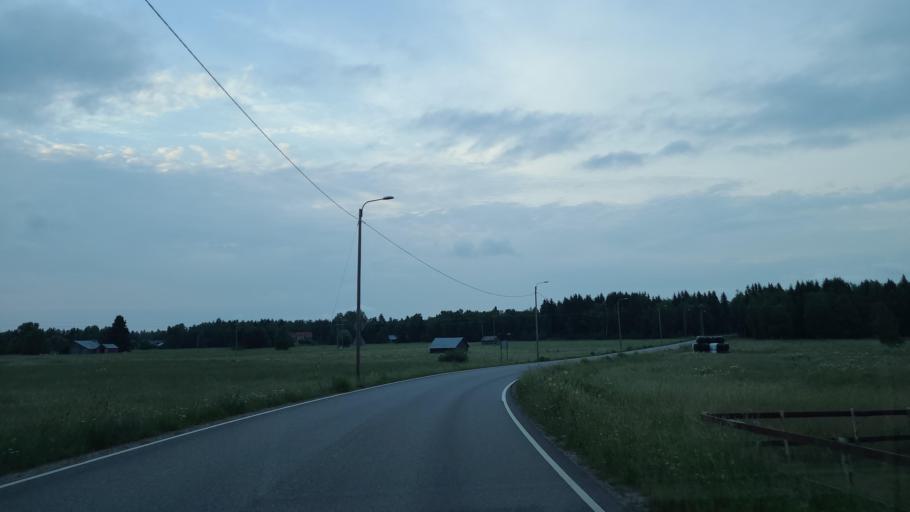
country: FI
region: Ostrobothnia
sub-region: Vaasa
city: Replot
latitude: 63.1972
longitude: 21.3067
